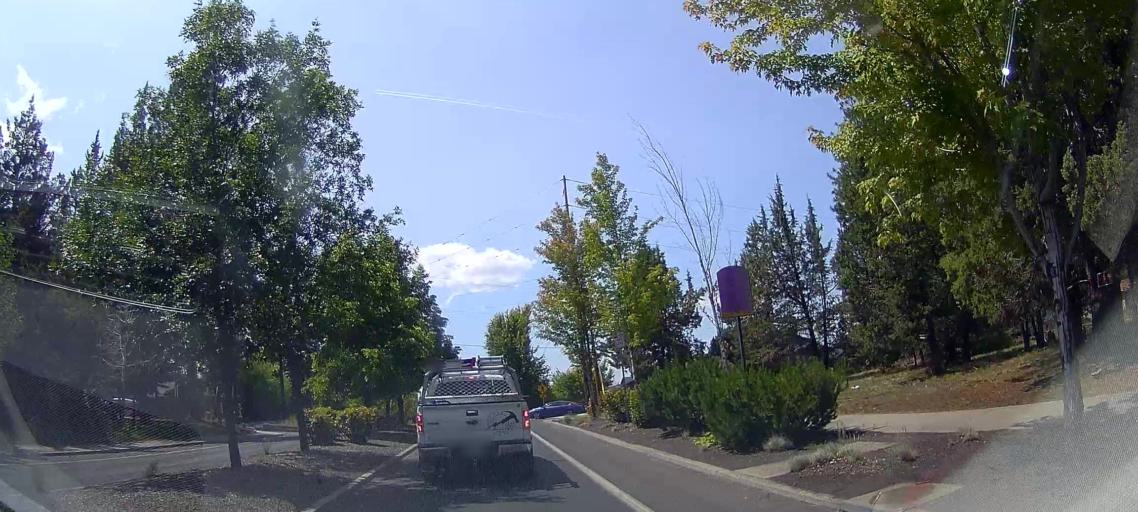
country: US
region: Oregon
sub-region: Deschutes County
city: Bend
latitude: 44.0397
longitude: -121.3131
